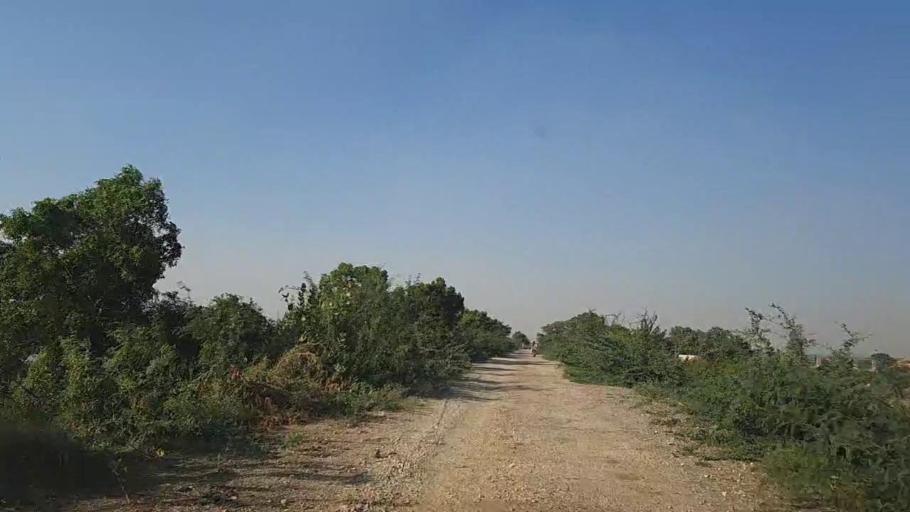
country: PK
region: Sindh
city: Daro Mehar
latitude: 25.0358
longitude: 68.1365
